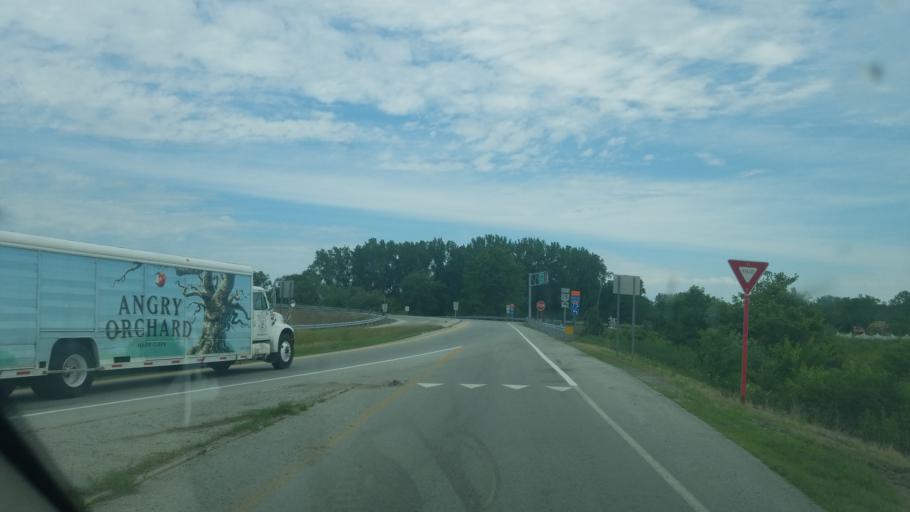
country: US
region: Ohio
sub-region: Wood County
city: North Baltimore
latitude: 41.2395
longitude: -83.6517
